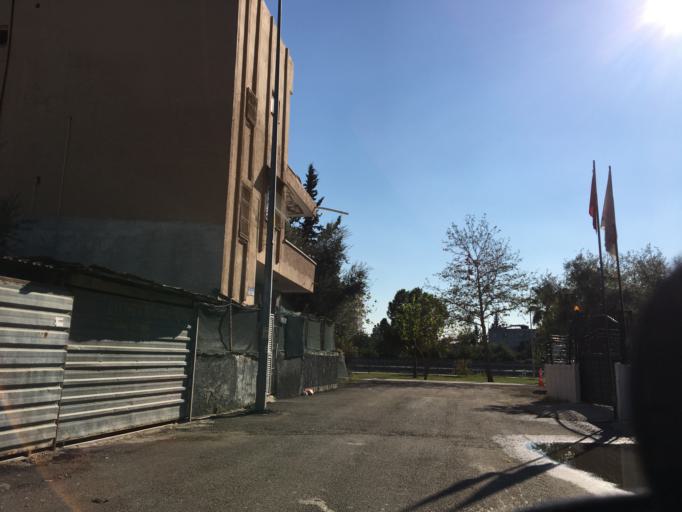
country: TR
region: Adana
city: Seyhan
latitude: 37.0117
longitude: 35.2915
